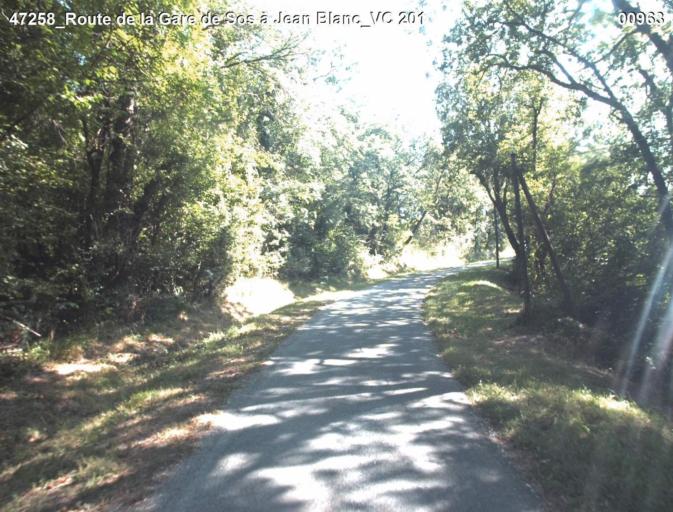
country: FR
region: Midi-Pyrenees
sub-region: Departement du Gers
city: Montreal
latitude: 44.0352
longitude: 0.1493
